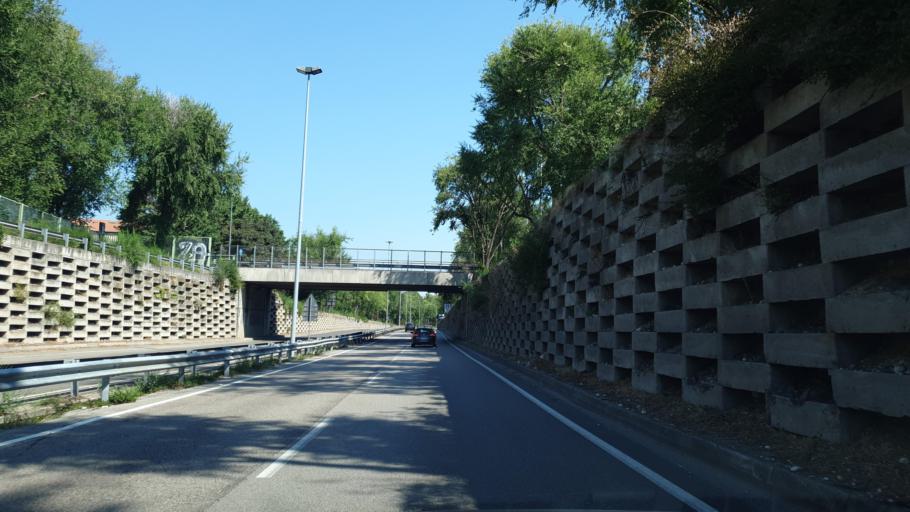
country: IT
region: Veneto
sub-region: Provincia di Verona
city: Verona
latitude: 45.4286
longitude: 10.9717
